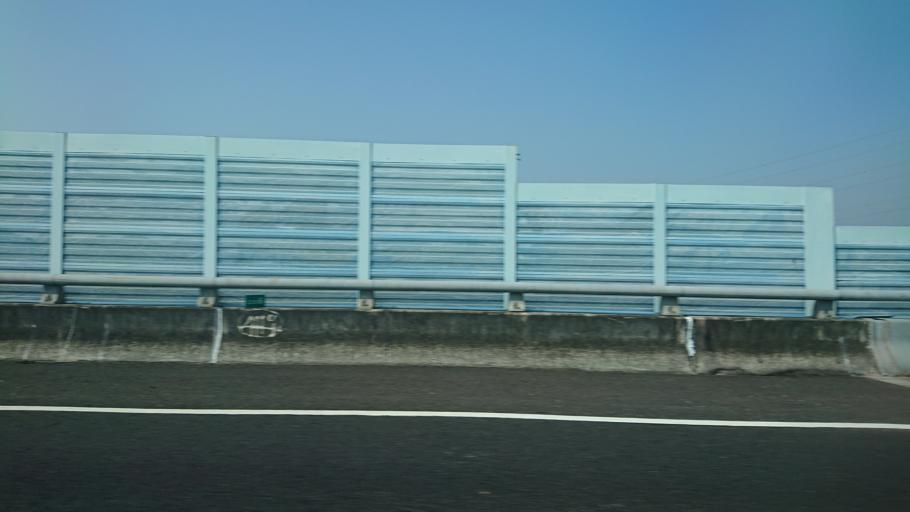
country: TW
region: Taiwan
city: Lugu
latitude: 23.8297
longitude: 120.7084
